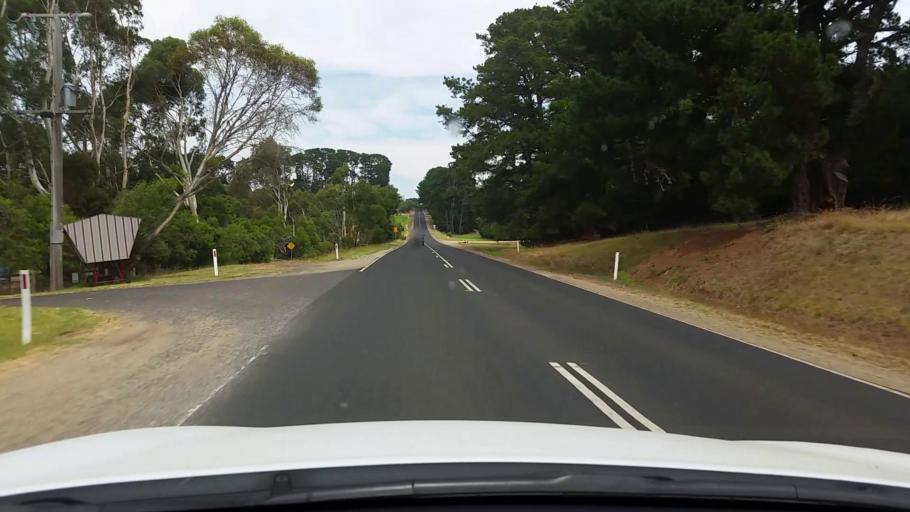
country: AU
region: Victoria
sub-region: Mornington Peninsula
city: Merricks
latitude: -38.4133
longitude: 145.0557
